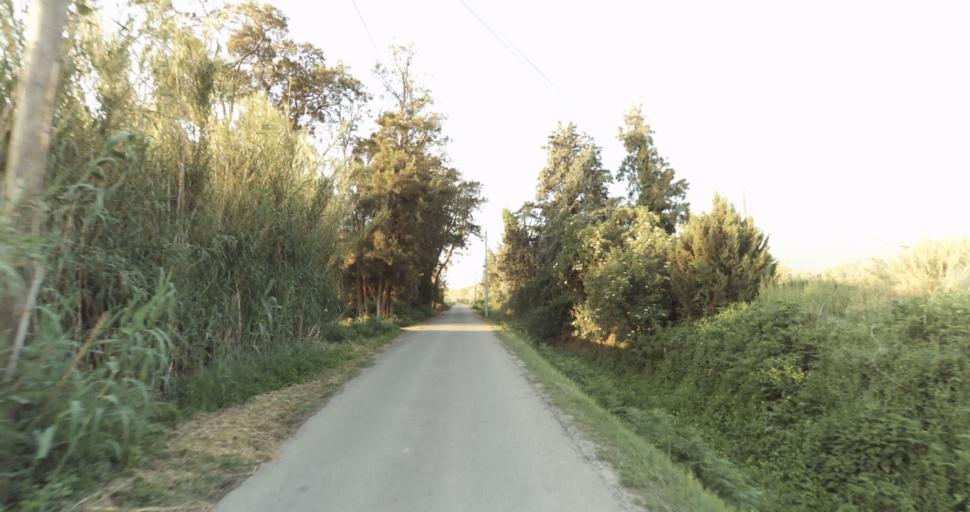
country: FR
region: Corsica
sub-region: Departement de la Haute-Corse
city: Biguglia
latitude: 42.6166
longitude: 9.4457
